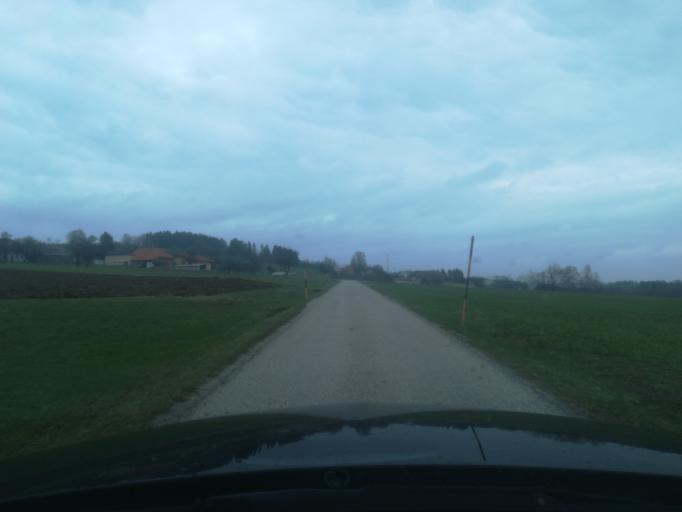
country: AT
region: Upper Austria
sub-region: Politischer Bezirk Rohrbach
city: Kleinzell im Muehlkreis
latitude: 48.3671
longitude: 13.9214
